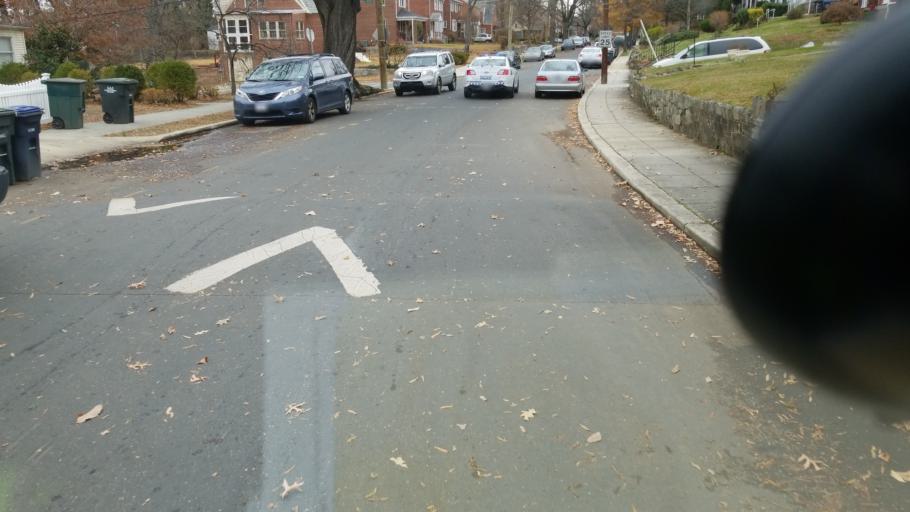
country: US
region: Maryland
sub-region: Prince George's County
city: Silver Hill
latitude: 38.8702
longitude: -76.9571
